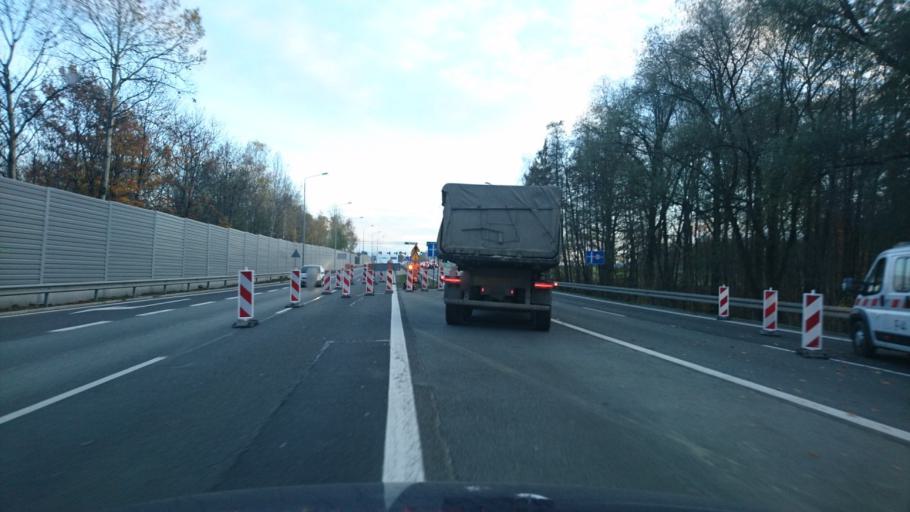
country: PL
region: Silesian Voivodeship
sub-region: Powiat bielski
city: Mazancowice
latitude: 49.8734
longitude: 19.0028
